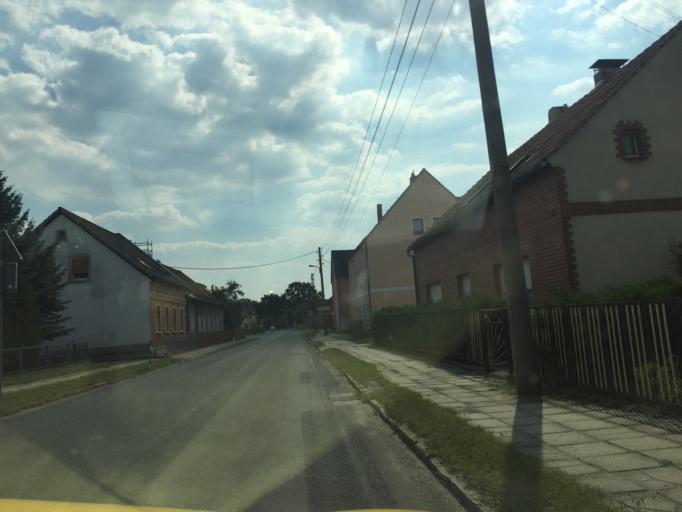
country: DE
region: Brandenburg
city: Welzow
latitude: 51.5739
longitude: 14.1730
